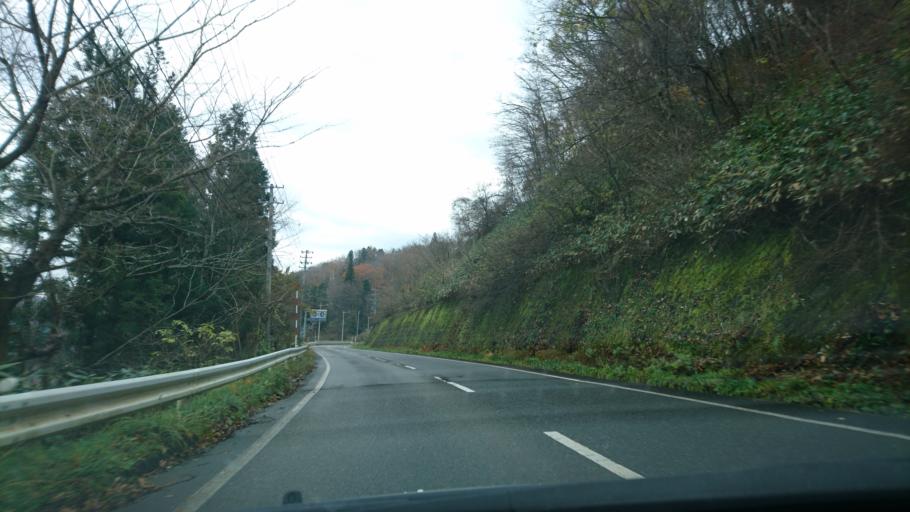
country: JP
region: Iwate
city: Ichinoseki
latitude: 38.9044
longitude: 140.9006
